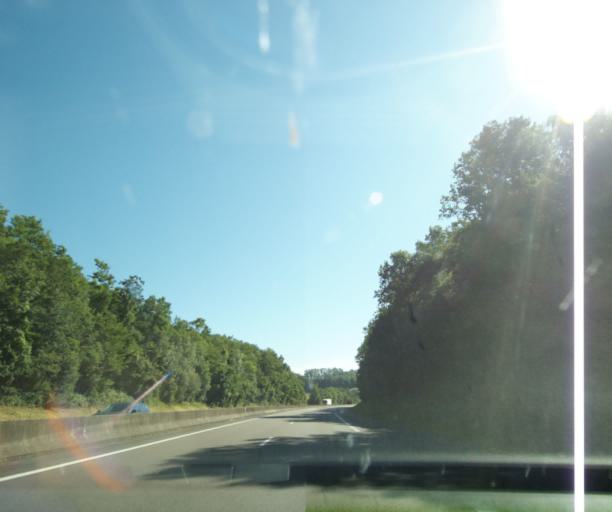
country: FR
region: Champagne-Ardenne
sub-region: Departement de la Haute-Marne
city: Avrecourt
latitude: 47.9573
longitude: 5.4458
